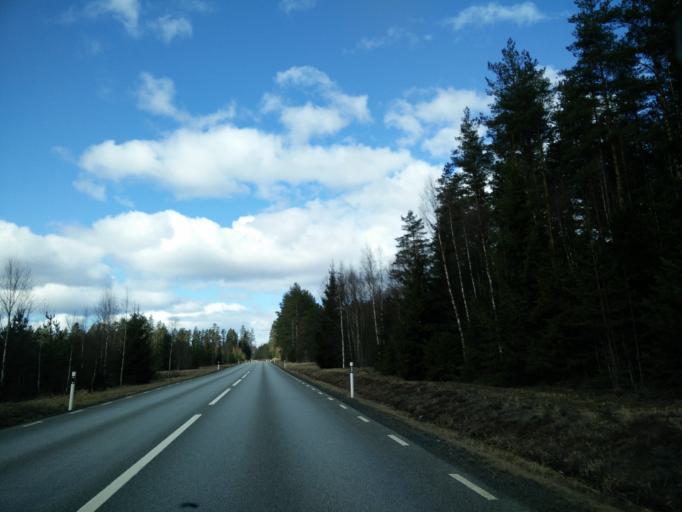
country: SE
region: Vaermland
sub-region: Munkfors Kommun
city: Munkfors
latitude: 59.9514
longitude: 13.5757
